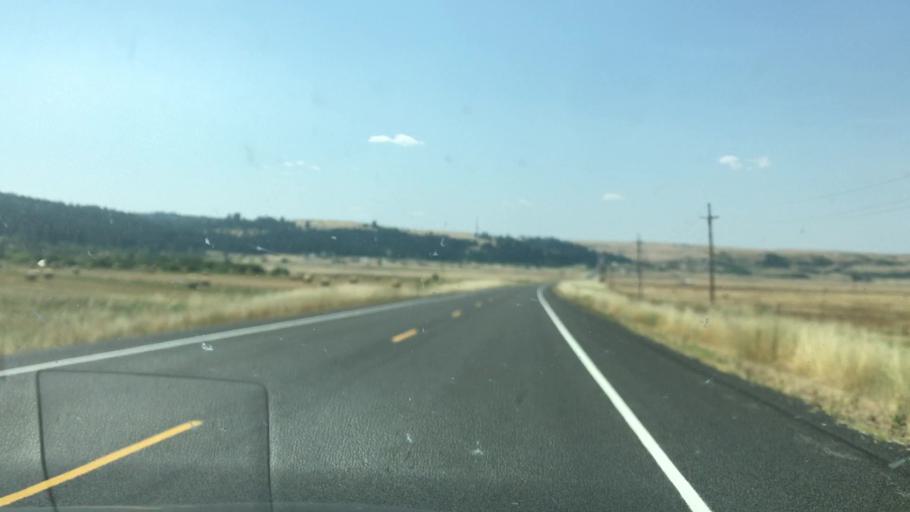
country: US
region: Idaho
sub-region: Idaho County
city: Grangeville
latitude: 45.8932
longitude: -116.1928
